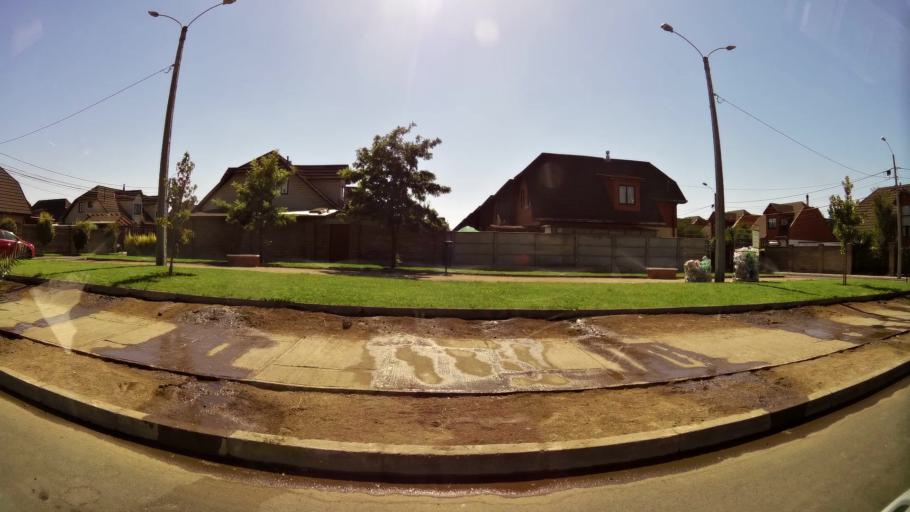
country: CL
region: Maule
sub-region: Provincia de Talca
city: Talca
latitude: -35.4295
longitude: -71.6156
